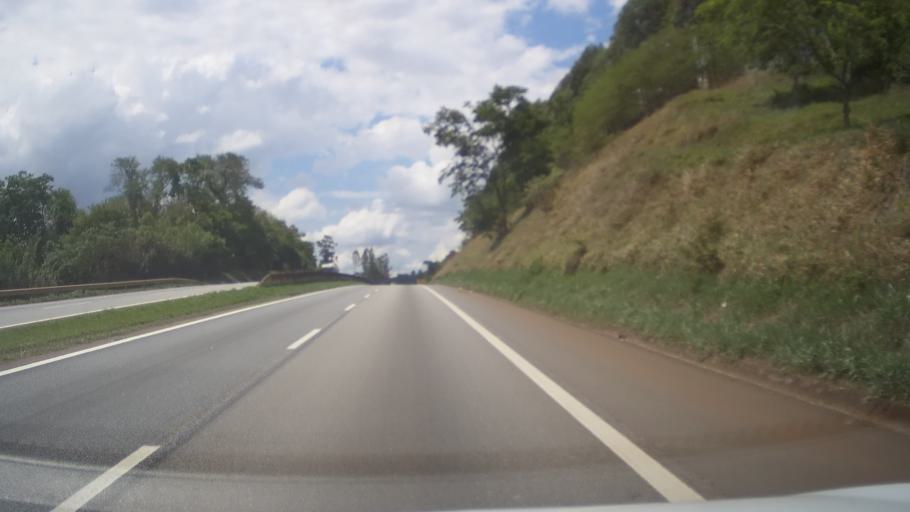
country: BR
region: Minas Gerais
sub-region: Nepomuceno
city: Nepomuceno
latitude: -21.2952
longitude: -45.1493
